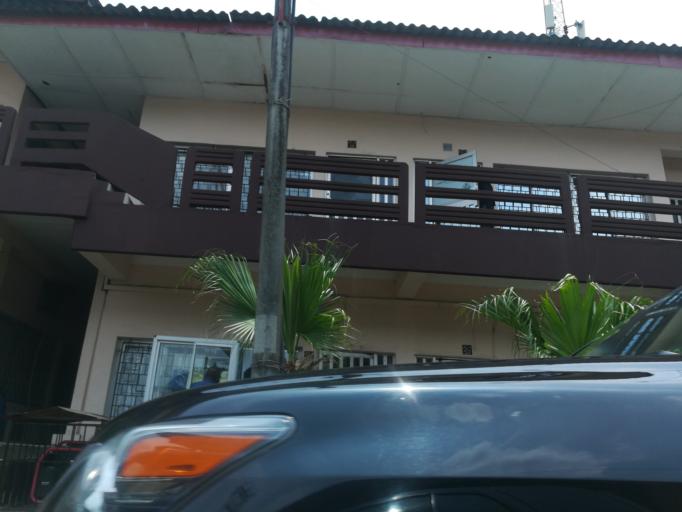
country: NG
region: Lagos
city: Lagos
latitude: 6.4548
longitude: 3.4046
